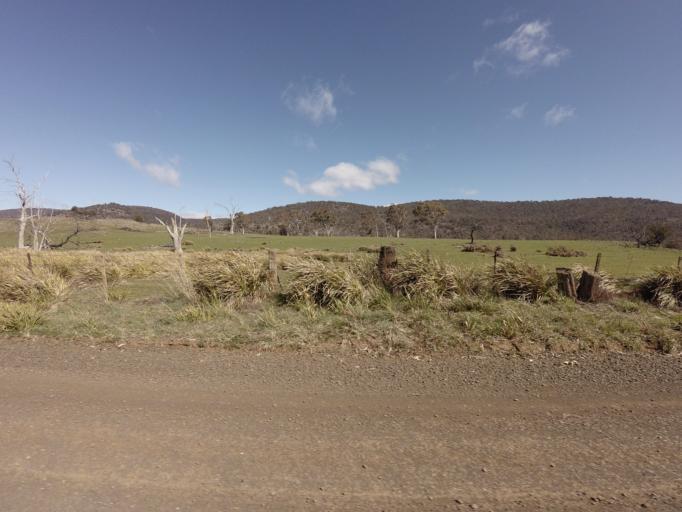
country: AU
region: Tasmania
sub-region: Northern Midlands
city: Evandale
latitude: -41.9403
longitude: 147.4240
